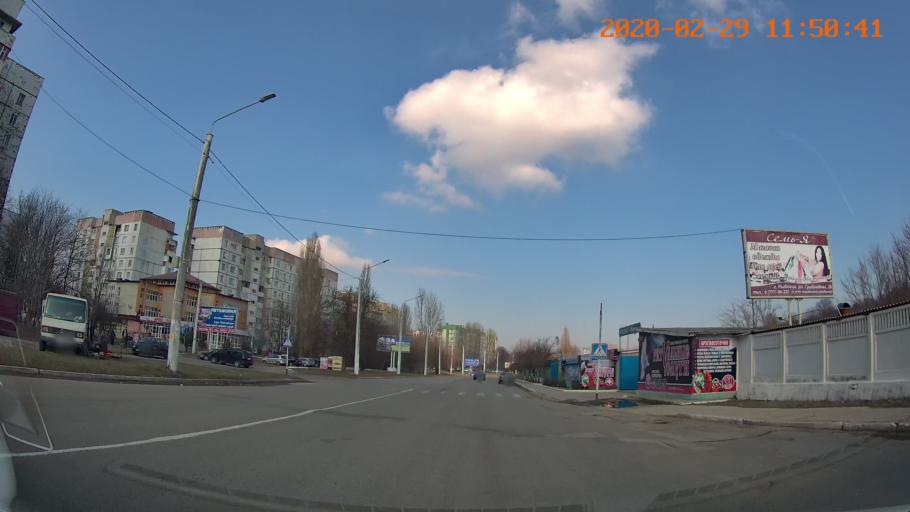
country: MD
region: Telenesti
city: Ribnita
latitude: 47.7600
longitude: 28.9901
